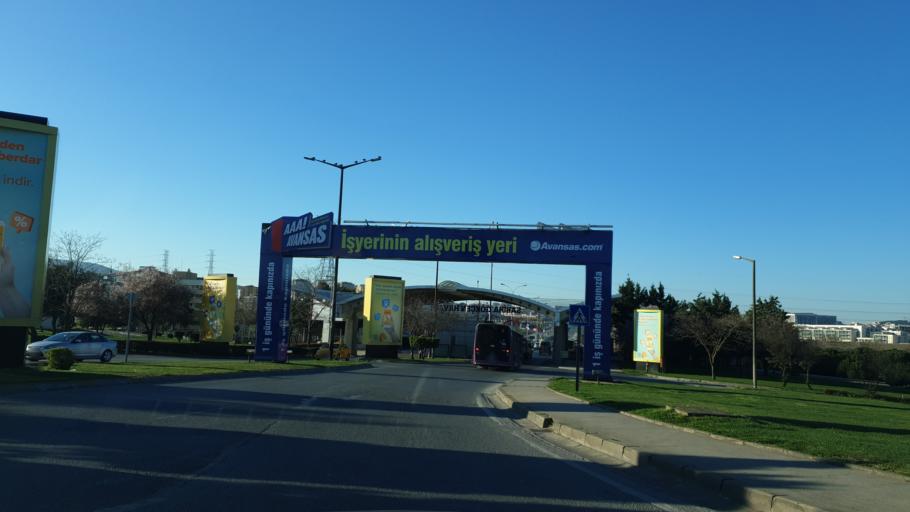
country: TR
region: Istanbul
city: Pendik
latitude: 40.9112
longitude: 29.3141
